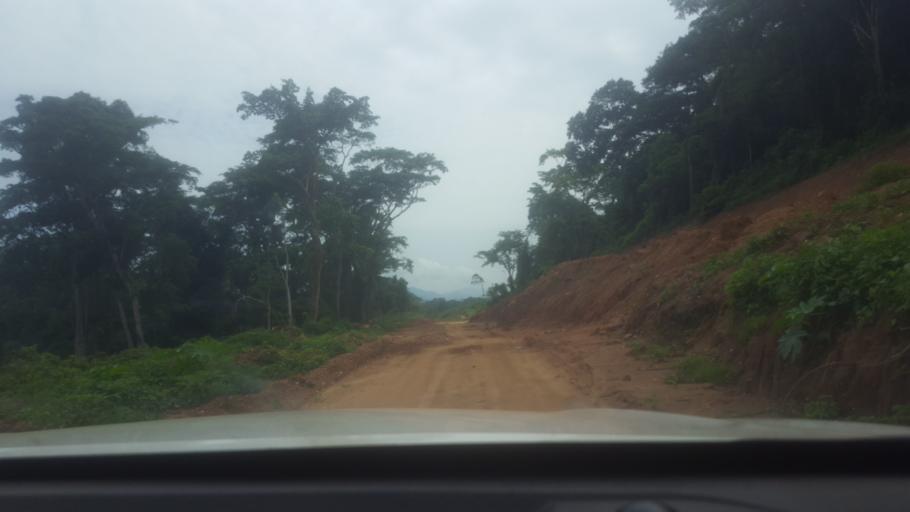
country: ET
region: Southern Nations, Nationalities, and People's Region
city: Tippi
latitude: 7.4839
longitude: 35.0349
